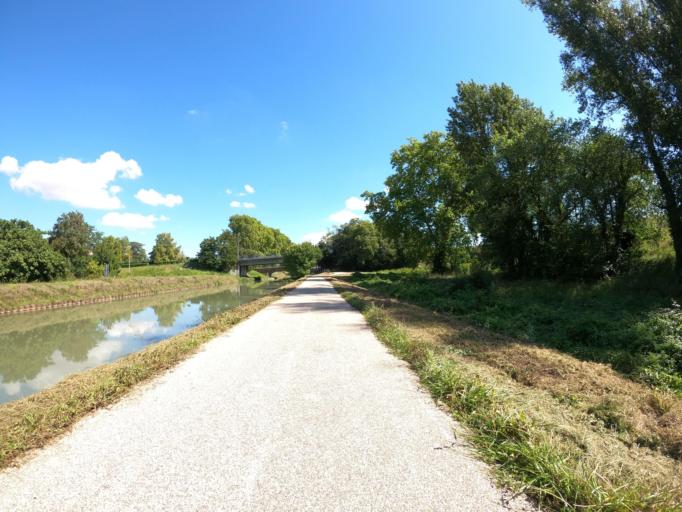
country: FR
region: Midi-Pyrenees
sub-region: Departement du Tarn-et-Garonne
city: Valence
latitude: 44.1041
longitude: 0.8911
